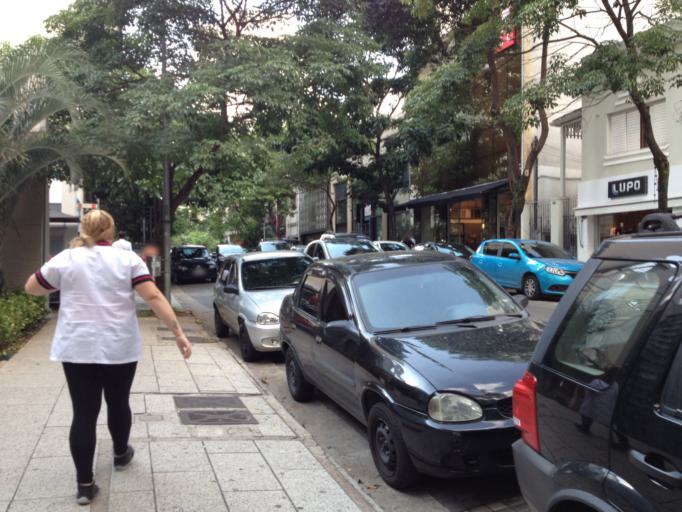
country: BR
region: Sao Paulo
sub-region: Sao Paulo
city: Sao Paulo
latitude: -23.5653
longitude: -46.6665
